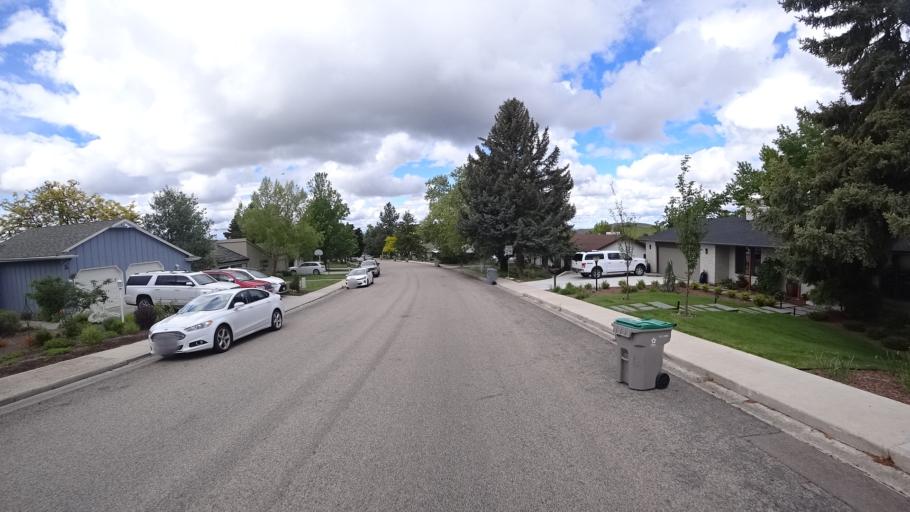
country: US
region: Idaho
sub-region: Ada County
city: Boise
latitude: 43.6517
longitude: -116.1816
